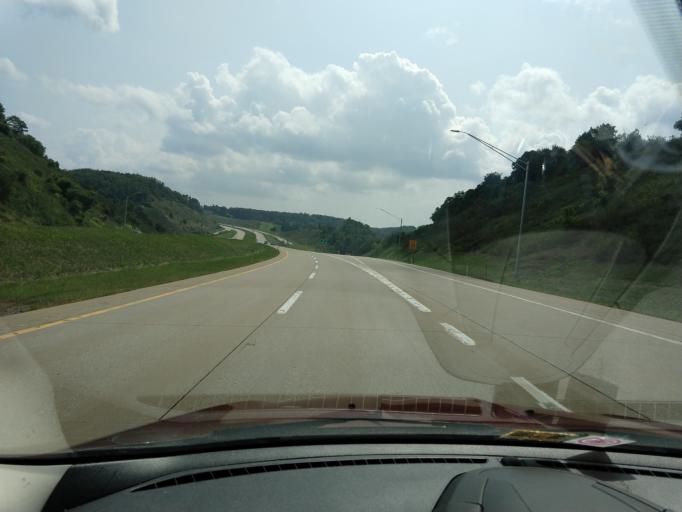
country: US
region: Pennsylvania
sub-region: Washington County
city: Gastonville
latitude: 40.2574
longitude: -79.9828
